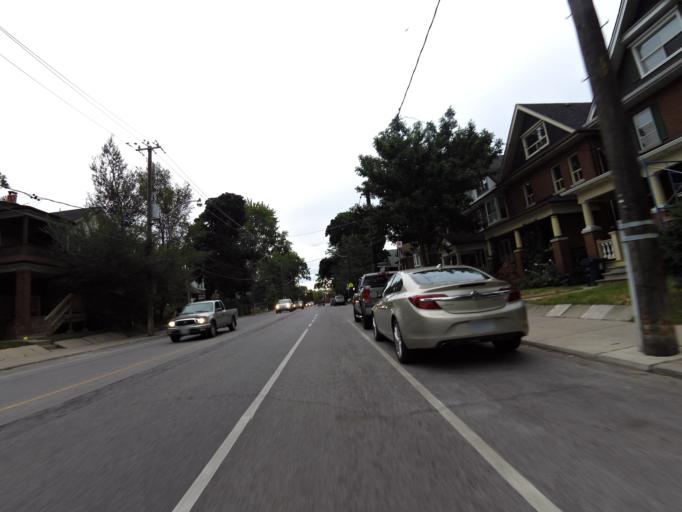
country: CA
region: Ontario
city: Toronto
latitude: 43.6607
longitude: -79.4770
